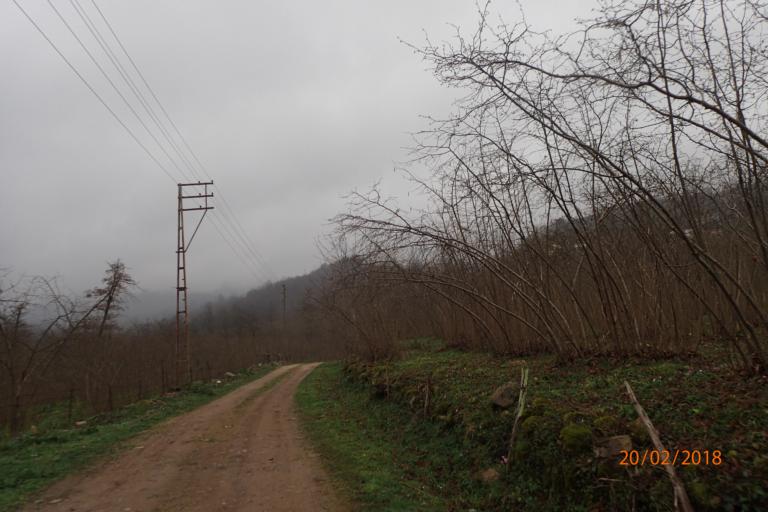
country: TR
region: Ordu
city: Camas
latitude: 40.9449
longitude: 37.5364
